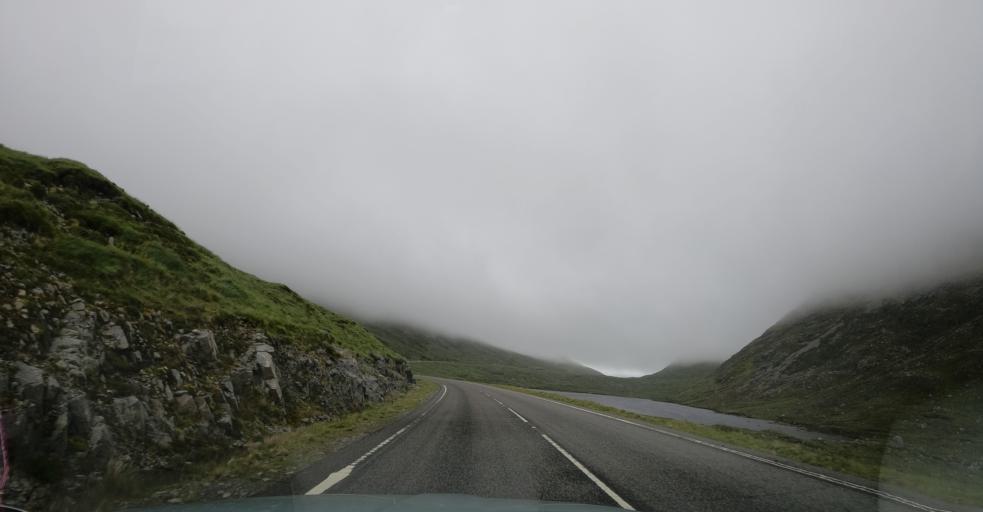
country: GB
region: Scotland
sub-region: Eilean Siar
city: Harris
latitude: 57.9410
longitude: -6.8201
